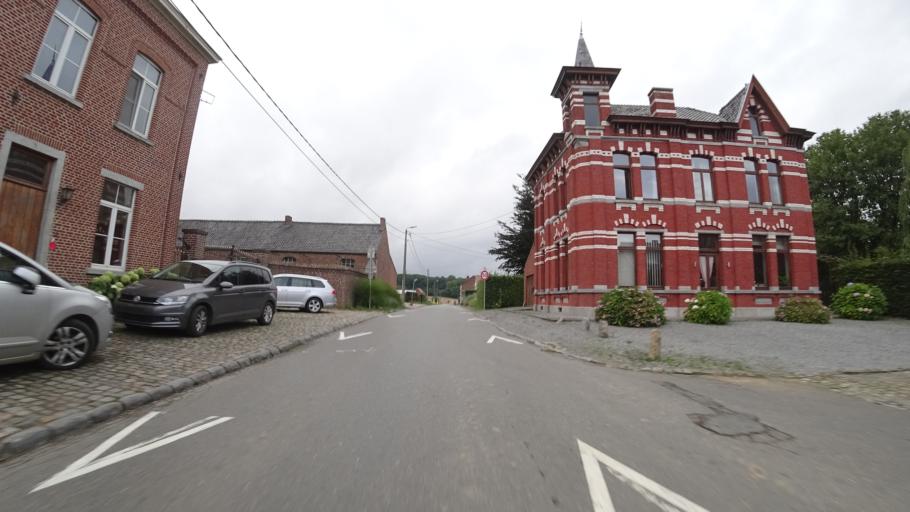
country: BE
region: Wallonia
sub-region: Province du Brabant Wallon
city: Walhain-Saint-Paul
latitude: 50.6021
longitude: 4.7474
